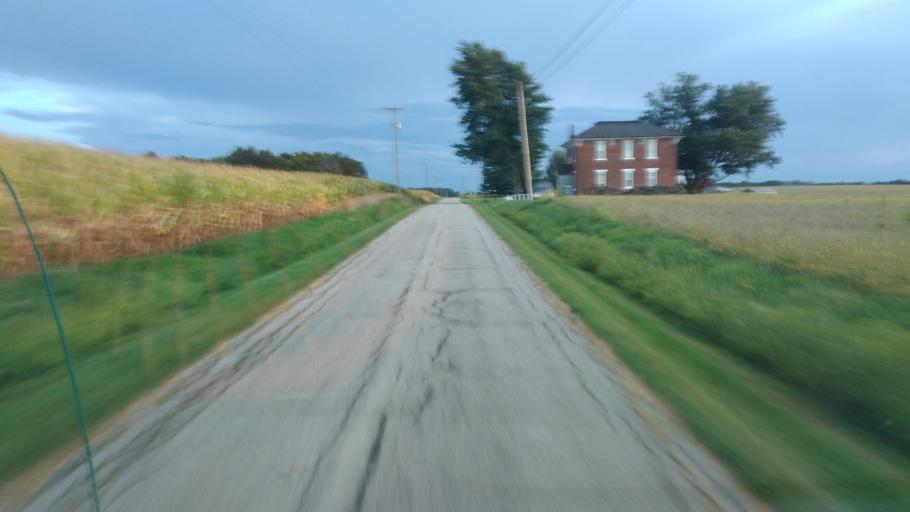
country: US
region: Ohio
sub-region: Crawford County
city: Bucyrus
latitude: 40.7117
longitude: -82.9188
